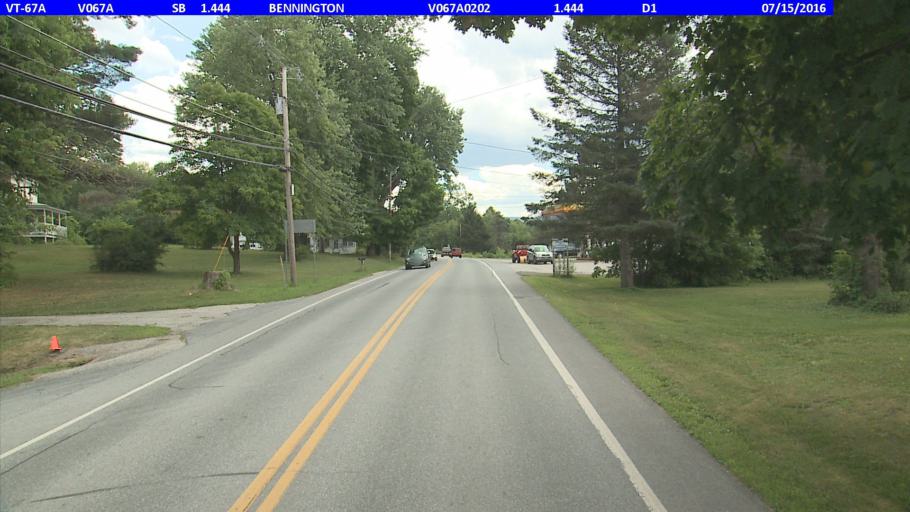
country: US
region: Vermont
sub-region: Bennington County
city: North Bennington
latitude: 42.9129
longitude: -73.2324
